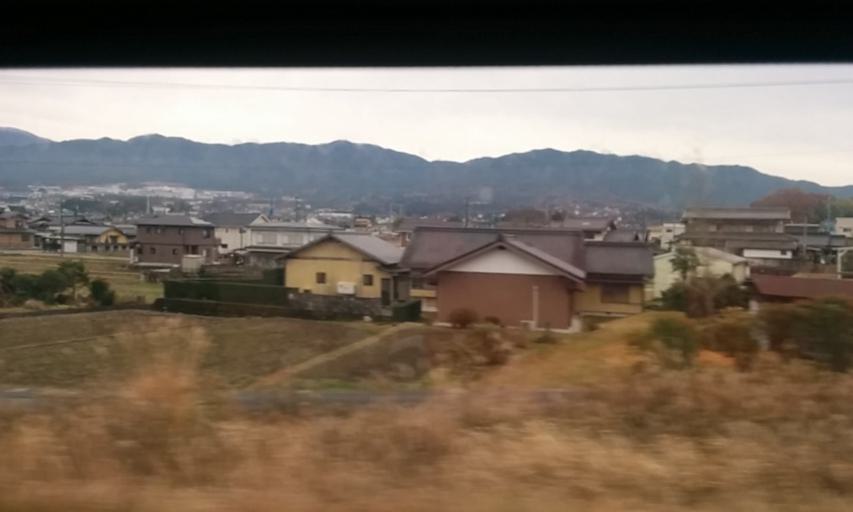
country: JP
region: Gifu
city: Nakatsugawa
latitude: 35.4747
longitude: 137.4397
